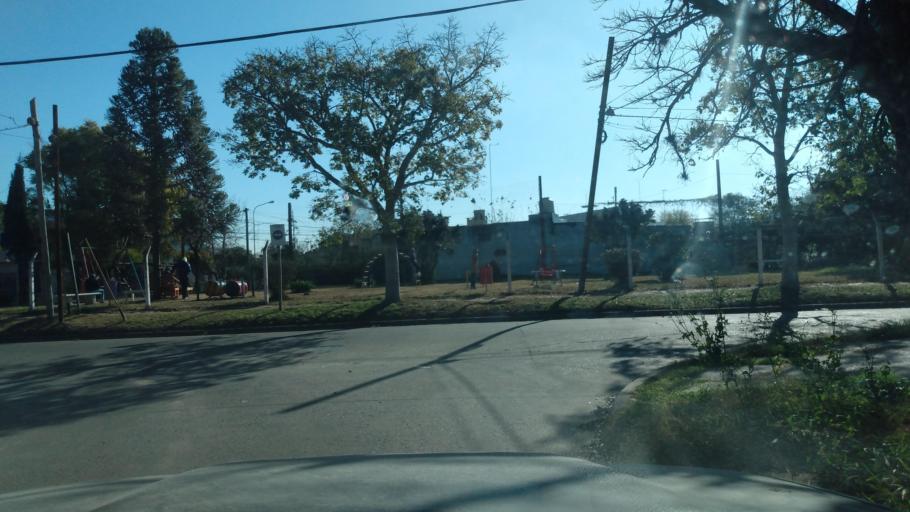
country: AR
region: Buenos Aires
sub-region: Partido de Lujan
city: Lujan
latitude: -34.5628
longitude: -59.1016
